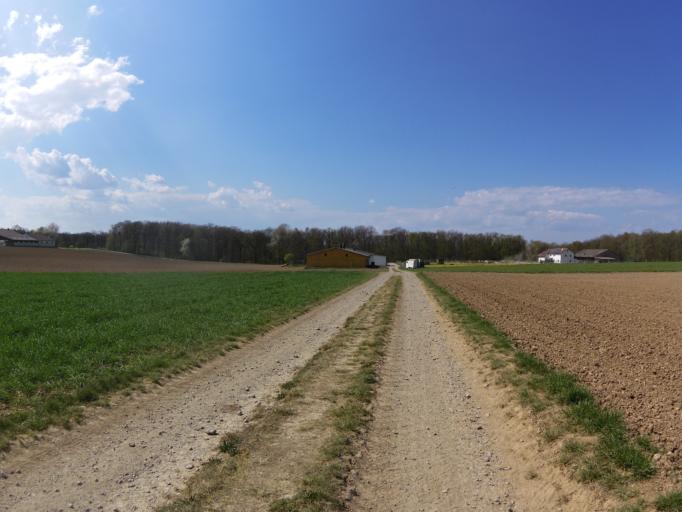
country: DE
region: Bavaria
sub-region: Regierungsbezirk Unterfranken
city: Oberpleichfeld
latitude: 49.8463
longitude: 10.0768
